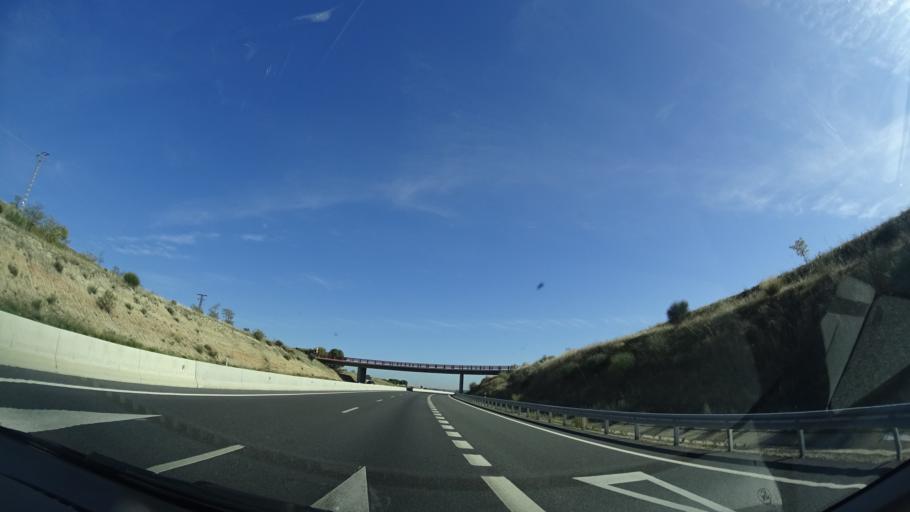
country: ES
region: Madrid
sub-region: Provincia de Madrid
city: Villanueva del Pardillo
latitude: 40.4824
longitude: -3.9238
